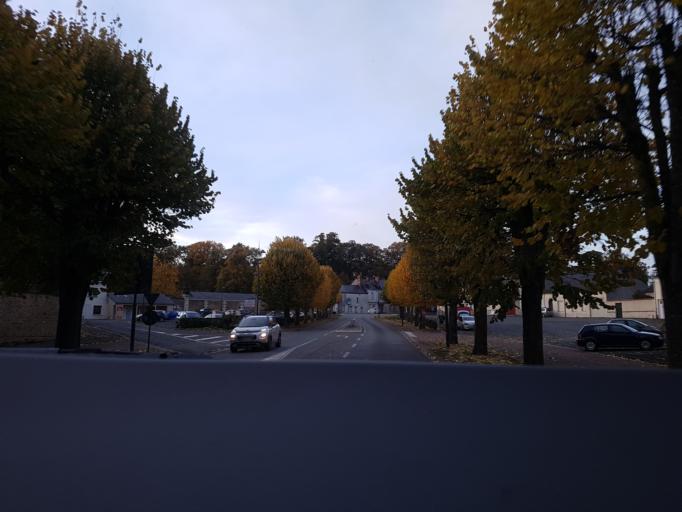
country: FR
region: Pays de la Loire
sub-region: Departement de la Mayenne
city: Craon
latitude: 47.8491
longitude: -0.9484
